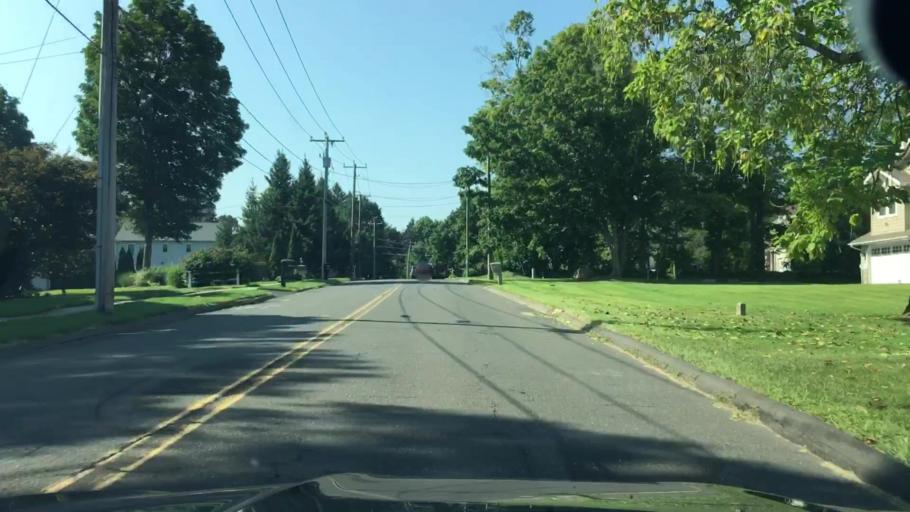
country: US
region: Connecticut
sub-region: New Haven County
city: Cheshire Village
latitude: 41.5207
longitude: -72.9150
